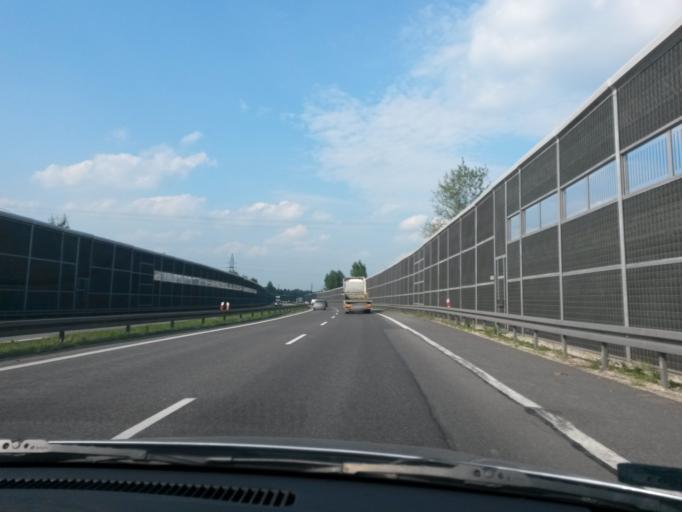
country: PL
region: Silesian Voivodeship
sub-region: Dabrowa Gornicza
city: Dabrowa Gornicza
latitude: 50.2743
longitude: 19.2083
